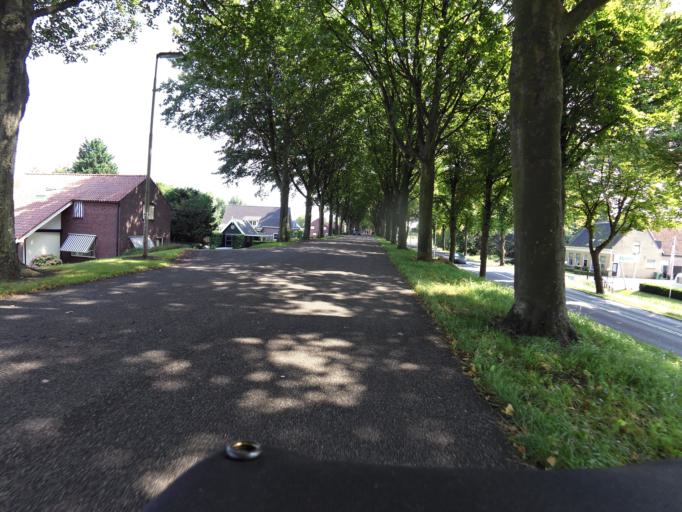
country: NL
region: South Holland
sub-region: Gemeente Oud-Beijerland
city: Oud-Beijerland
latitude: 51.8220
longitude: 4.4337
